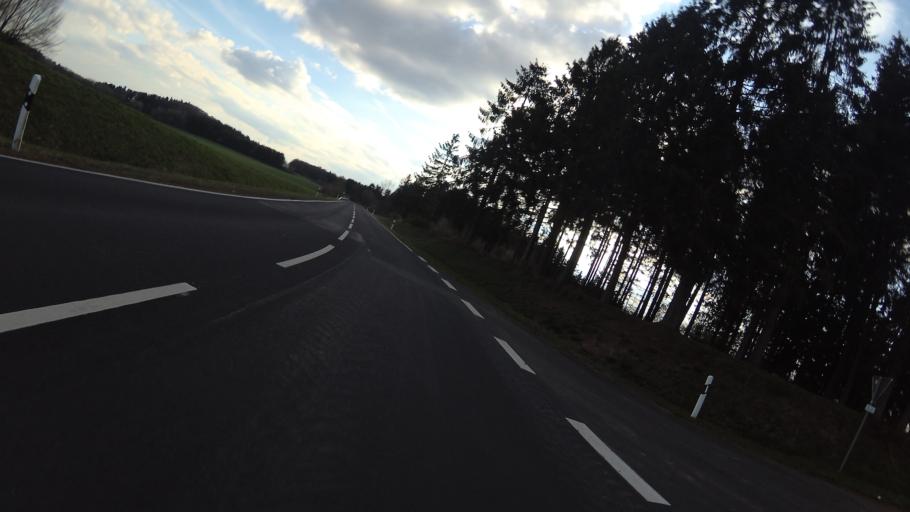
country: DE
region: Rheinland-Pfalz
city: Sarmersbach
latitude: 50.2392
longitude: 6.8952
